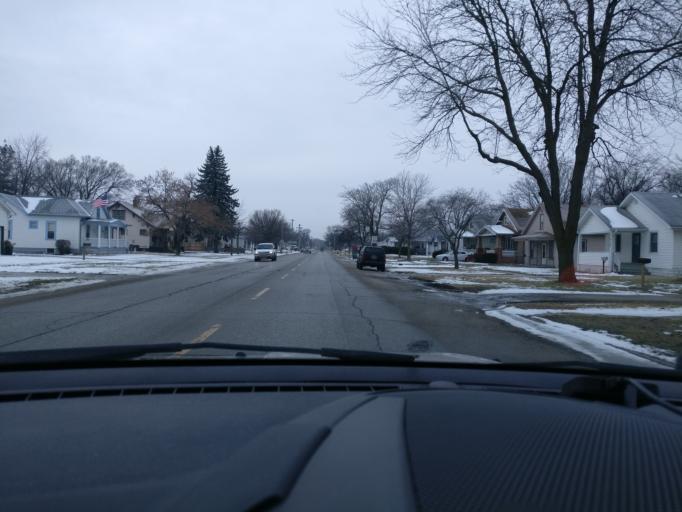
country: US
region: Nebraska
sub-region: Dodge County
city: Fremont
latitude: 41.4363
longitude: -96.5064
